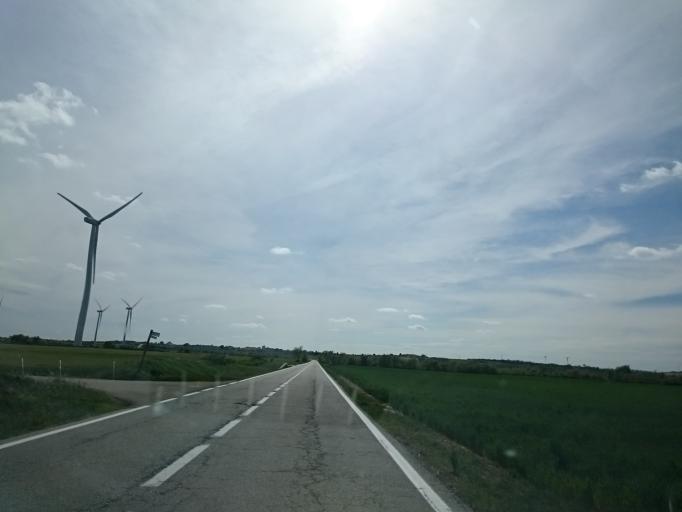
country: ES
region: Catalonia
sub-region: Provincia de Lleida
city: Sant Guim de Freixenet
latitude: 41.6703
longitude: 1.4466
